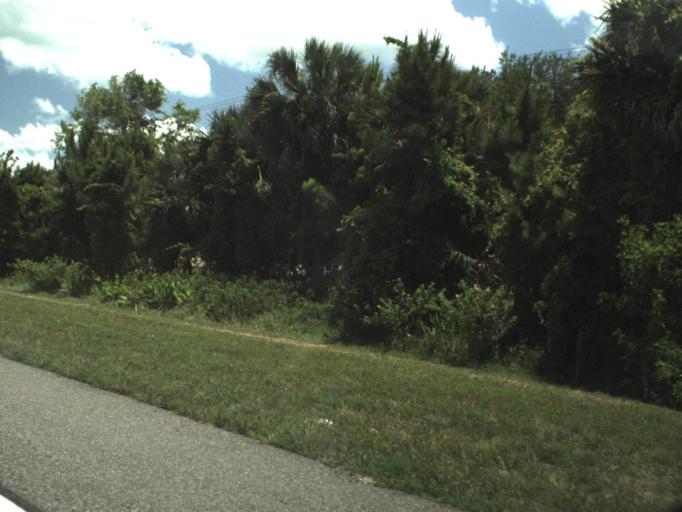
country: US
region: Florida
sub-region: Brevard County
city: Cape Canaveral
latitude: 28.4050
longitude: -80.6703
